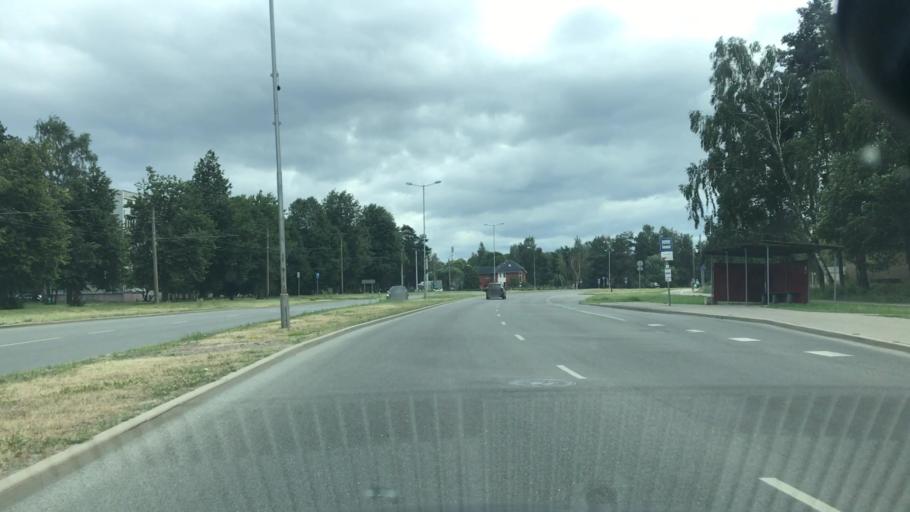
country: LV
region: Marupe
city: Marupe
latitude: 56.9592
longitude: 24.0215
